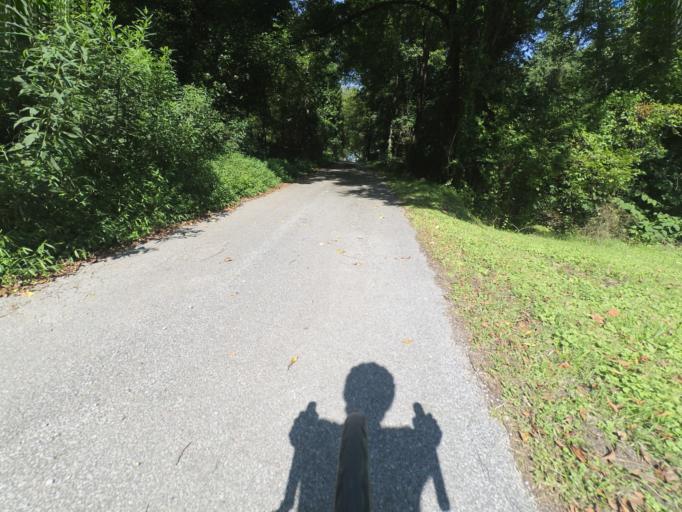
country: US
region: West Virginia
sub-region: Cabell County
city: Huntington
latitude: 38.3871
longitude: -82.4724
